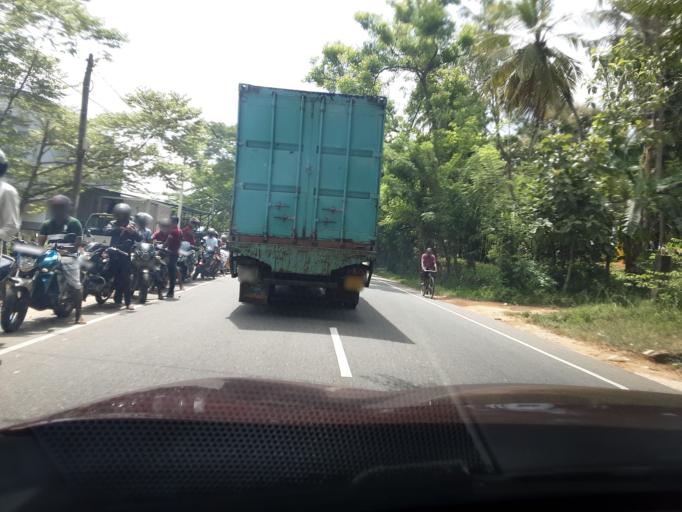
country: LK
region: North Western
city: Kuliyapitiya
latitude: 7.4491
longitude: 80.1986
